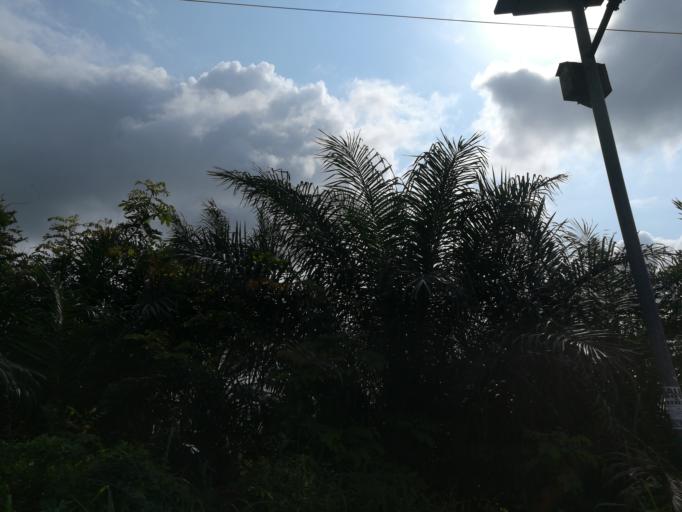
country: NG
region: Rivers
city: Okrika
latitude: 4.7534
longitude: 7.0847
